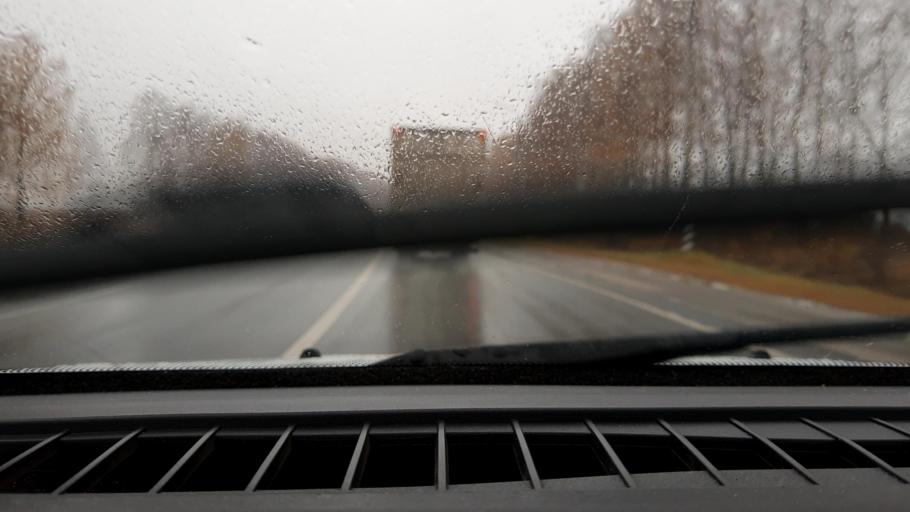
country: RU
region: Nizjnij Novgorod
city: Linda
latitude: 56.5637
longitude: 44.0242
